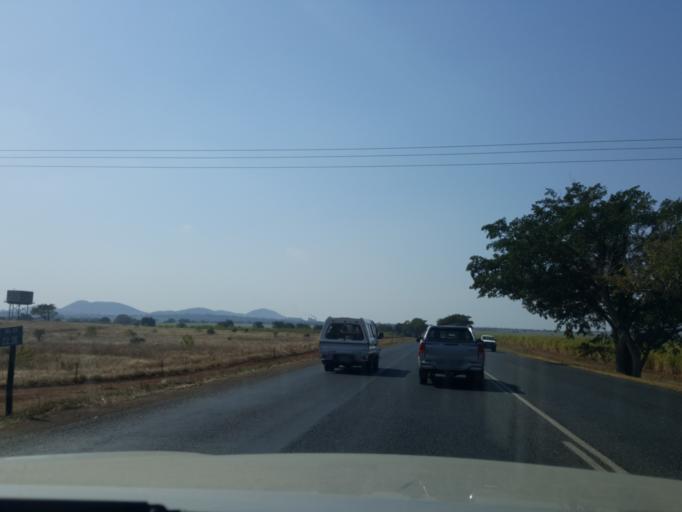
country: SZ
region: Hhohho
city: Ntfonjeni
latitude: -25.4925
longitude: 31.5241
